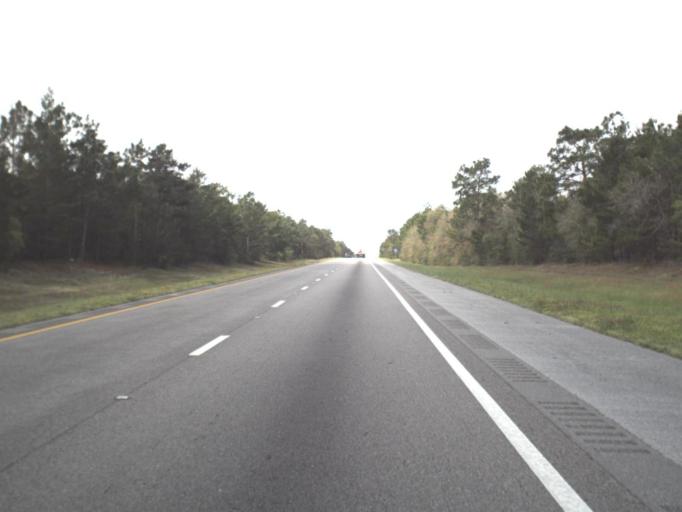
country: US
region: Florida
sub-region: Okaloosa County
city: Crestview
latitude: 30.7291
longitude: -86.3938
